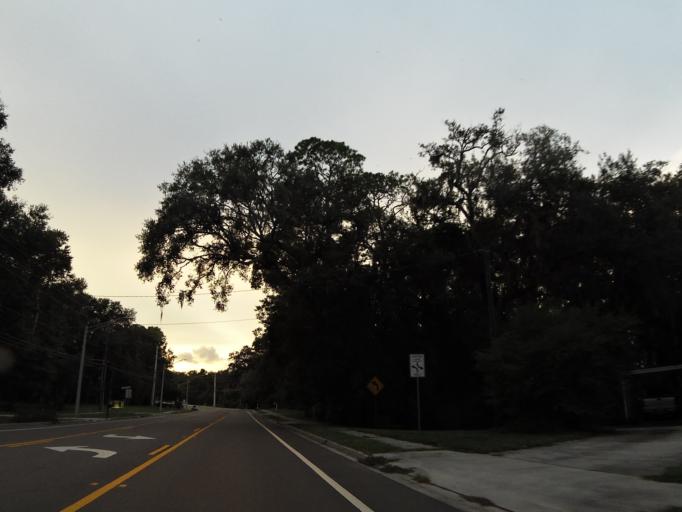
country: US
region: Florida
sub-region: Duval County
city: Jacksonville
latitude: 30.3654
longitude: -81.5572
